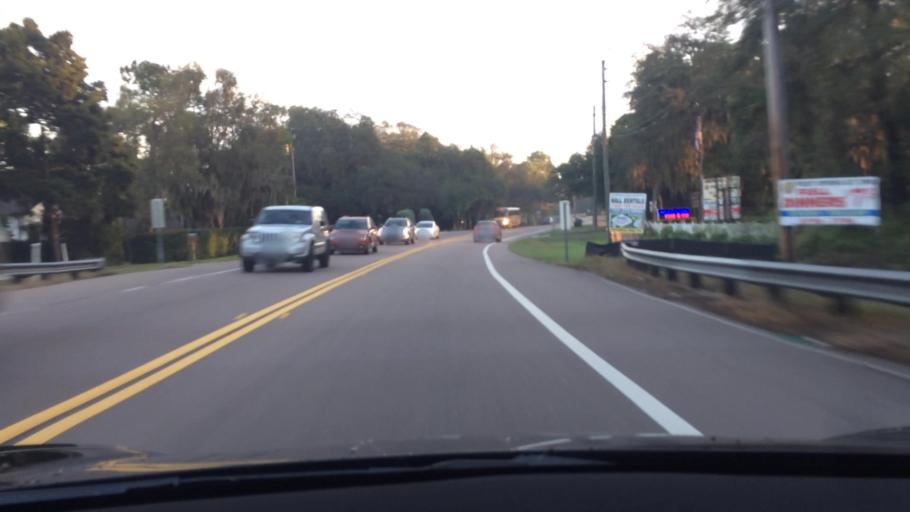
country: US
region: Florida
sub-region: Hillsborough County
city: Citrus Park
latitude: 28.1234
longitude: -82.5773
